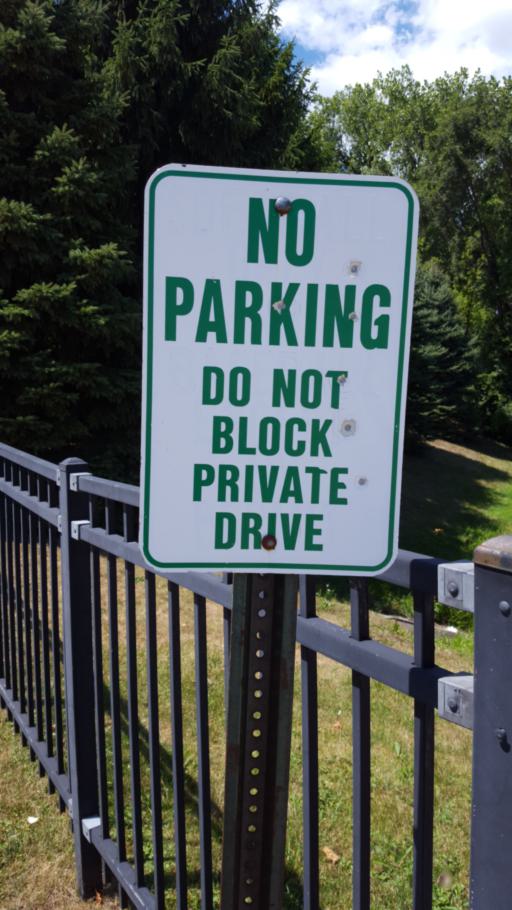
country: US
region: Illinois
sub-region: Cook County
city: Northfield
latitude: 42.0985
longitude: -87.8052
